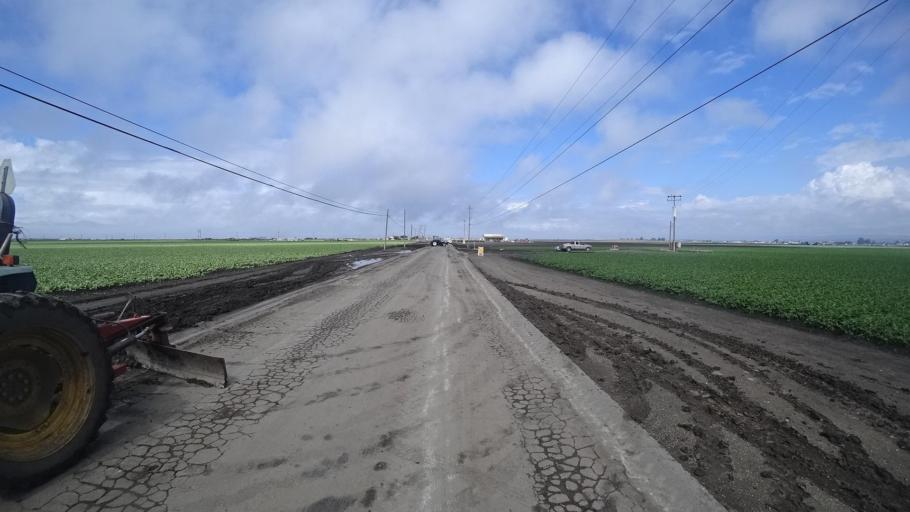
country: US
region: California
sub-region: Monterey County
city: Castroville
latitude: 36.7380
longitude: -121.7623
